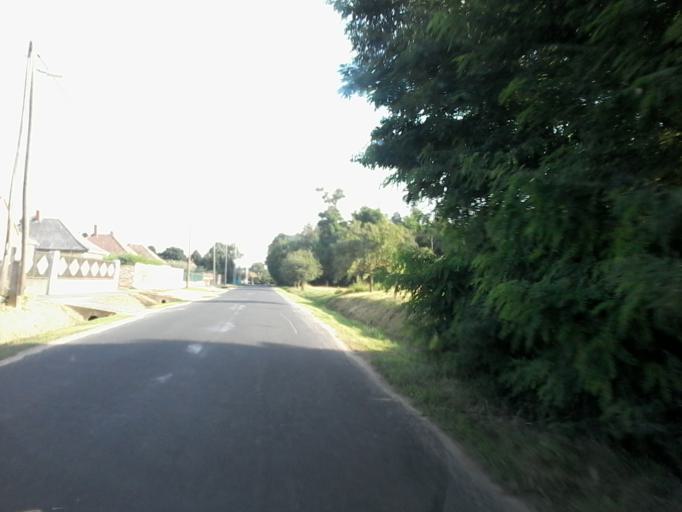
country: HU
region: Vas
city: Celldomolk
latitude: 47.1955
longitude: 17.1090
